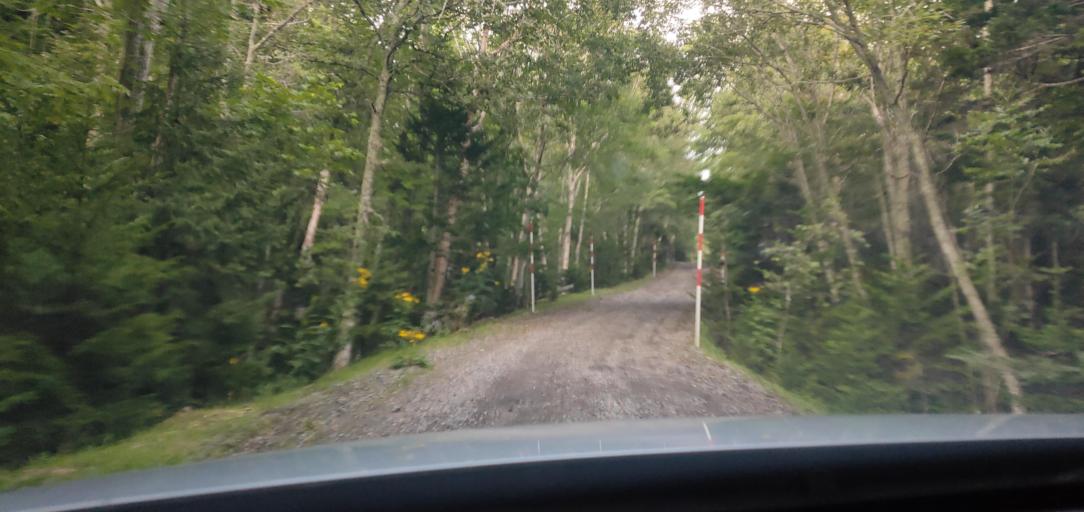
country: JP
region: Hokkaido
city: Kitami
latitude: 43.3749
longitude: 143.9670
